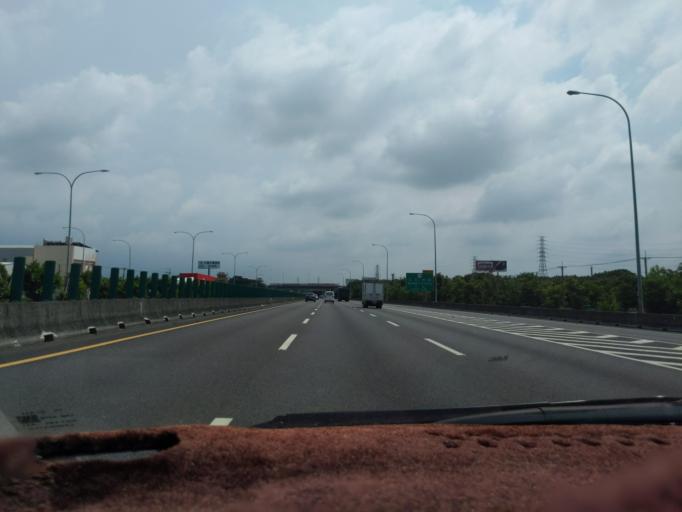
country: TW
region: Taiwan
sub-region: Nantou
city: Nantou
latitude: 23.8896
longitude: 120.4933
